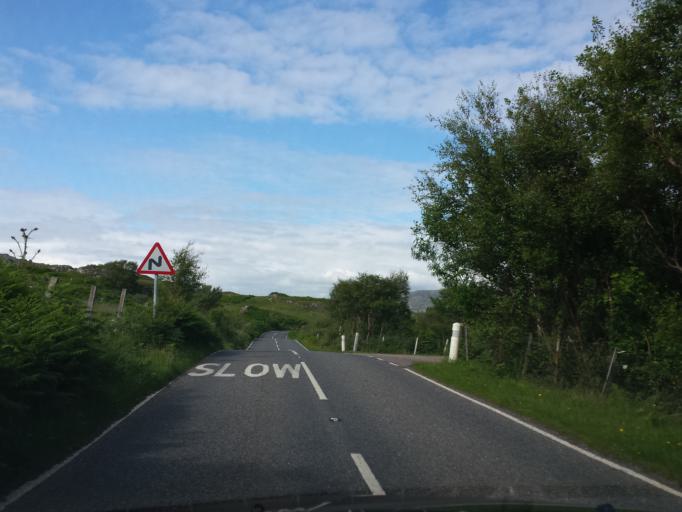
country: GB
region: Scotland
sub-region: Argyll and Bute
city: Isle Of Mull
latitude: 56.9616
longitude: -5.8350
